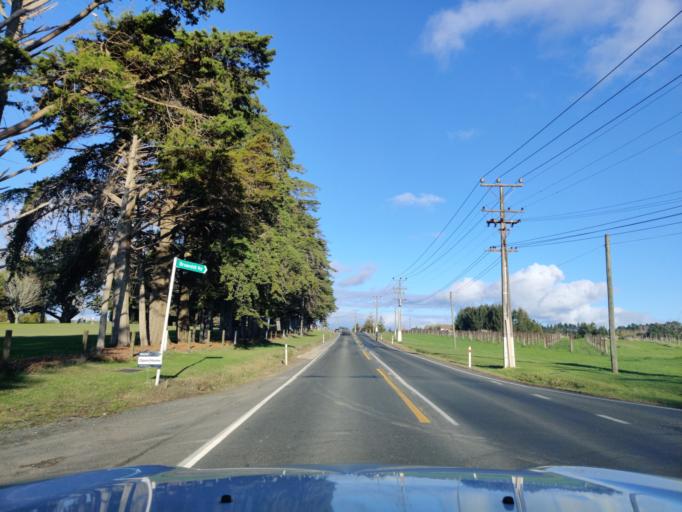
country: NZ
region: Auckland
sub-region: Auckland
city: Pakuranga
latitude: -36.9563
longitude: 174.9698
